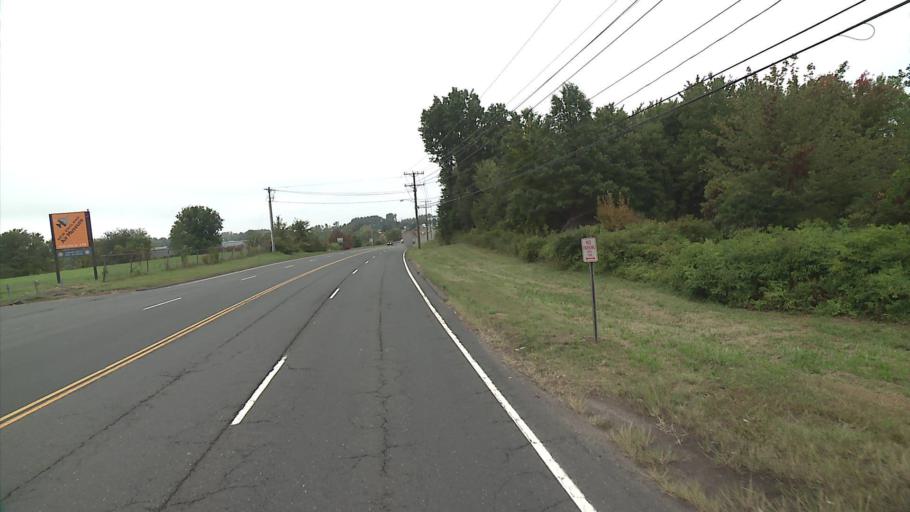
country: US
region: Connecticut
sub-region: Hartford County
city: Suffield Depot
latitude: 41.9560
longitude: -72.6645
